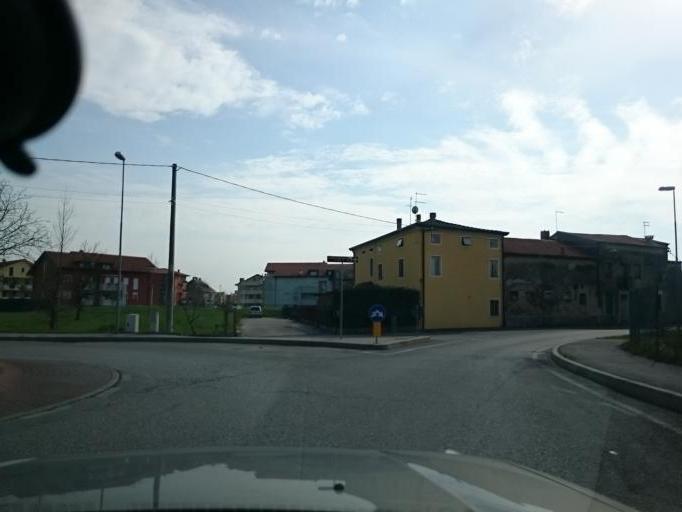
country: IT
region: Veneto
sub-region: Provincia di Padova
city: Mandriola-Sant'Agostino
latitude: 45.3701
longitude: 11.8692
